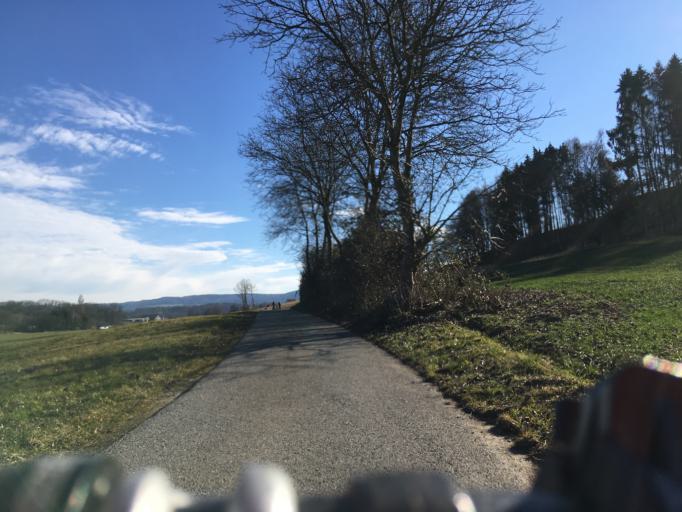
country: CH
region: Schaffhausen
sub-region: Bezirk Stein
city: Ramsen
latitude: 47.6946
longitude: 8.8113
